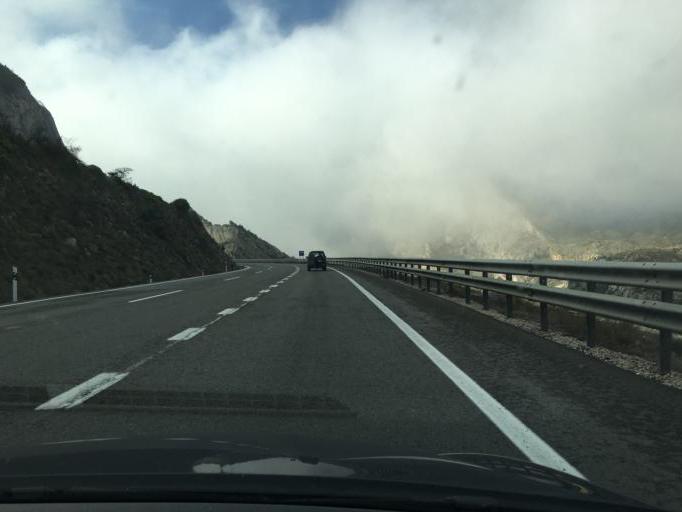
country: ES
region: Castille and Leon
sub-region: Provincia de Burgos
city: Pancorbo
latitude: 42.6385
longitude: -3.1024
